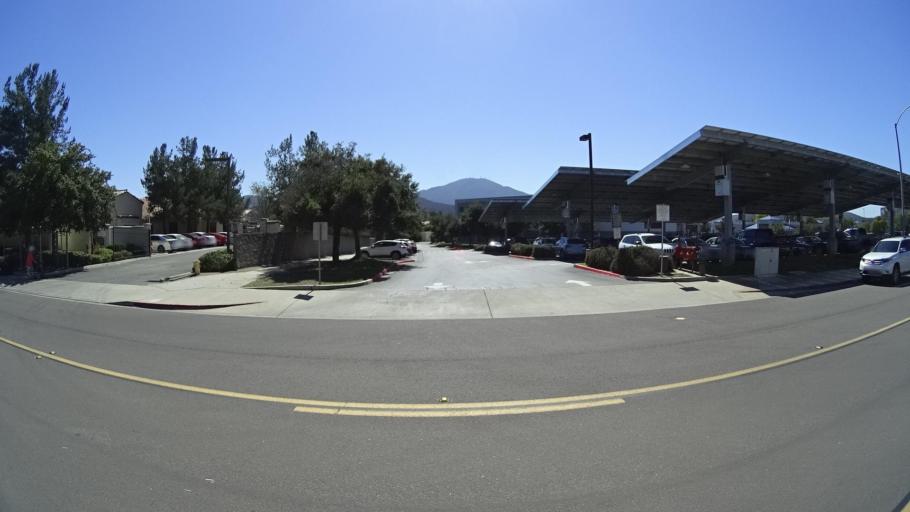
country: US
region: California
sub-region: San Diego County
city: Rancho San Diego
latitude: 32.7495
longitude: -116.9313
